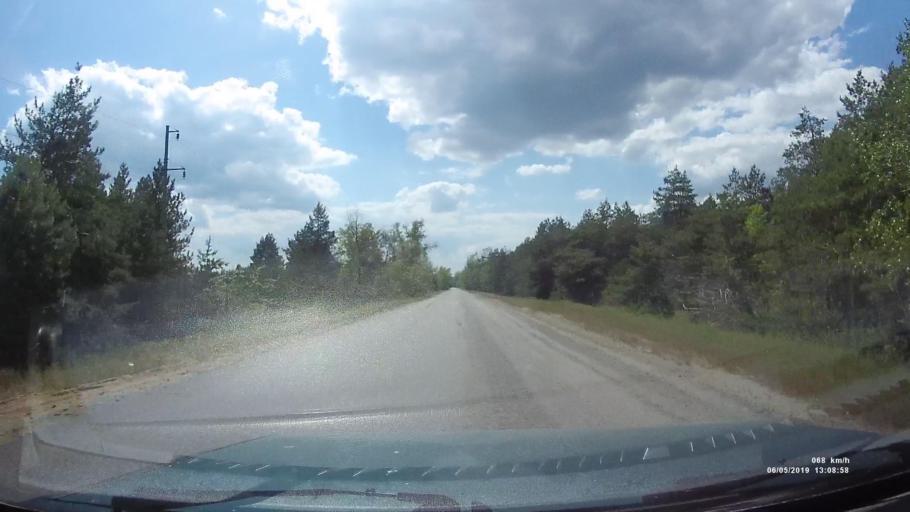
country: RU
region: Rostov
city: Ust'-Donetskiy
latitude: 47.7720
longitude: 40.9897
